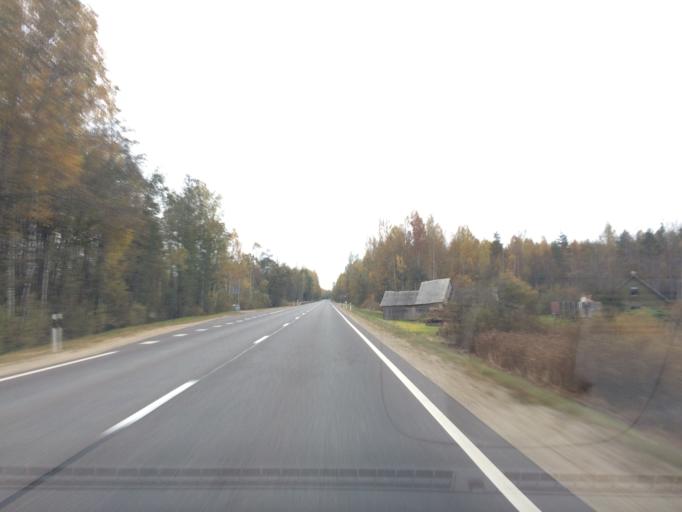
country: LV
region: Livani
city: Livani
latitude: 56.5436
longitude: 26.1223
